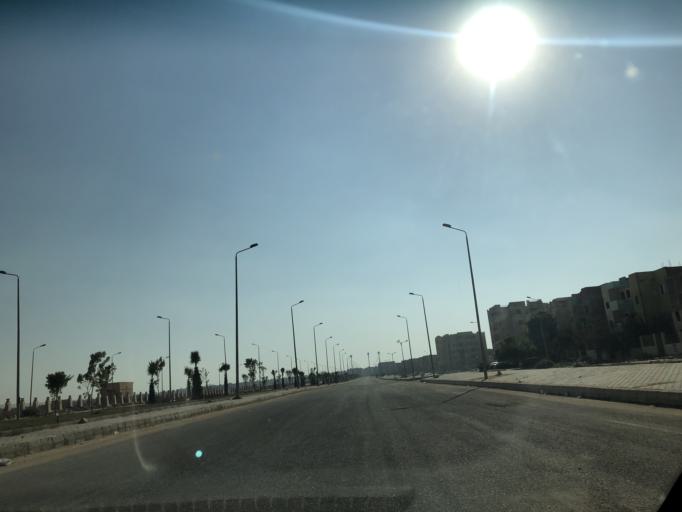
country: EG
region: Al Jizah
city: Madinat Sittah Uktubar
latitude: 29.9274
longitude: 31.0681
